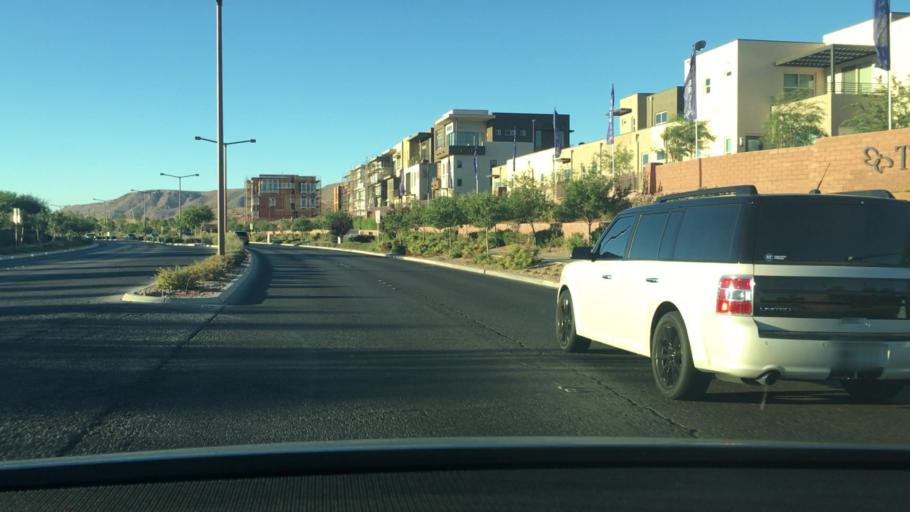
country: US
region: Nevada
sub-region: Clark County
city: Summerlin South
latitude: 36.1130
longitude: -115.3299
